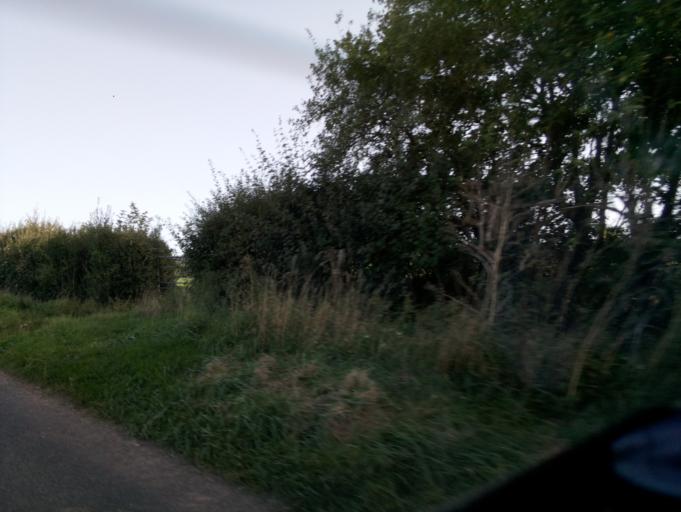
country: GB
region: England
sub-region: Gloucestershire
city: Gloucester
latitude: 51.9613
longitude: -2.2918
